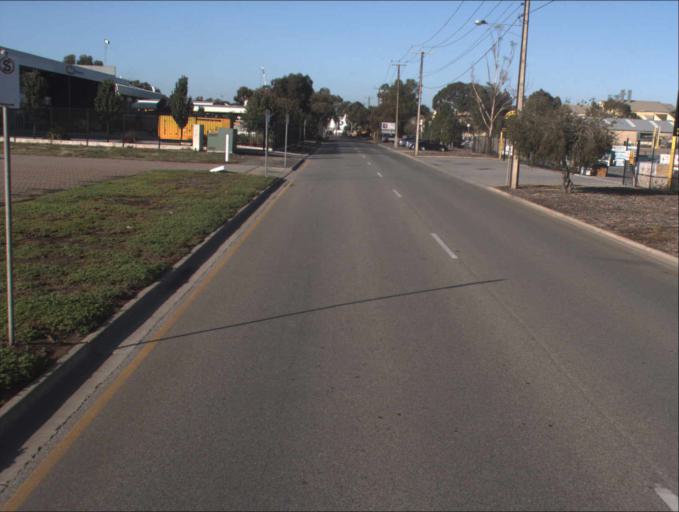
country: AU
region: South Australia
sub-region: Port Adelaide Enfield
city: Blair Athol
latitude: -34.8494
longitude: 138.5851
